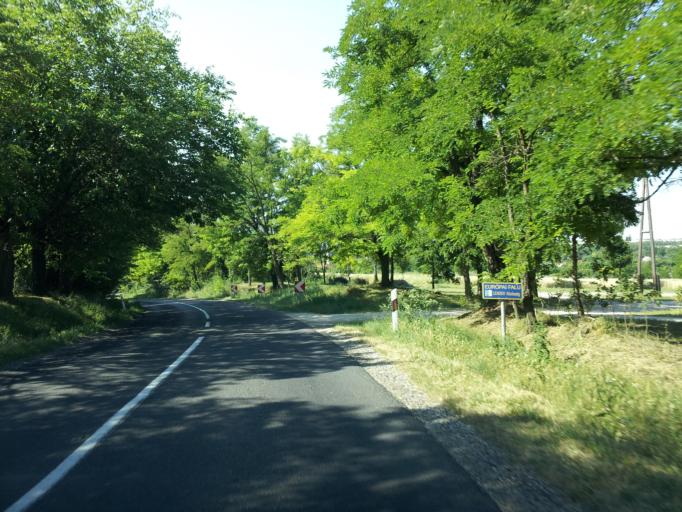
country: HU
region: Fejer
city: Lovasbereny
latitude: 47.3777
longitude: 18.5816
